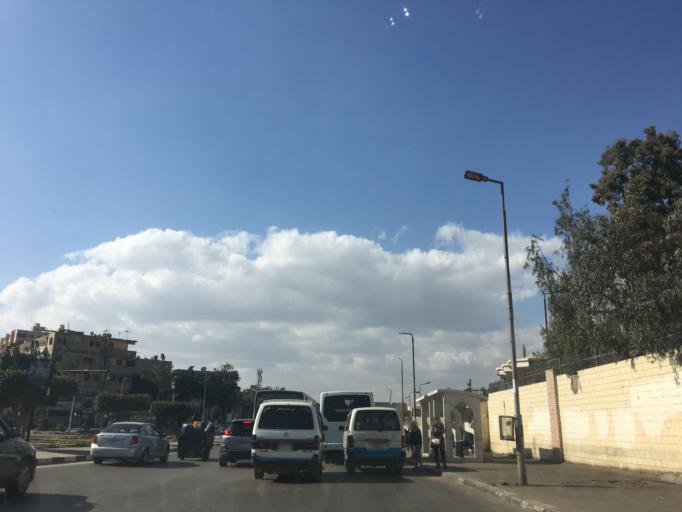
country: EG
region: Muhafazat al Qahirah
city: Cairo
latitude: 30.0503
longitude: 31.3157
